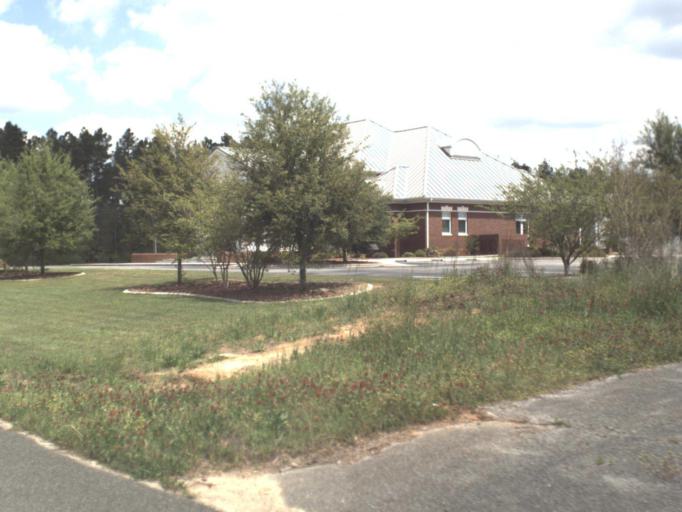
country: US
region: Florida
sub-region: Okaloosa County
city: Crestview
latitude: 30.8534
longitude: -86.6750
